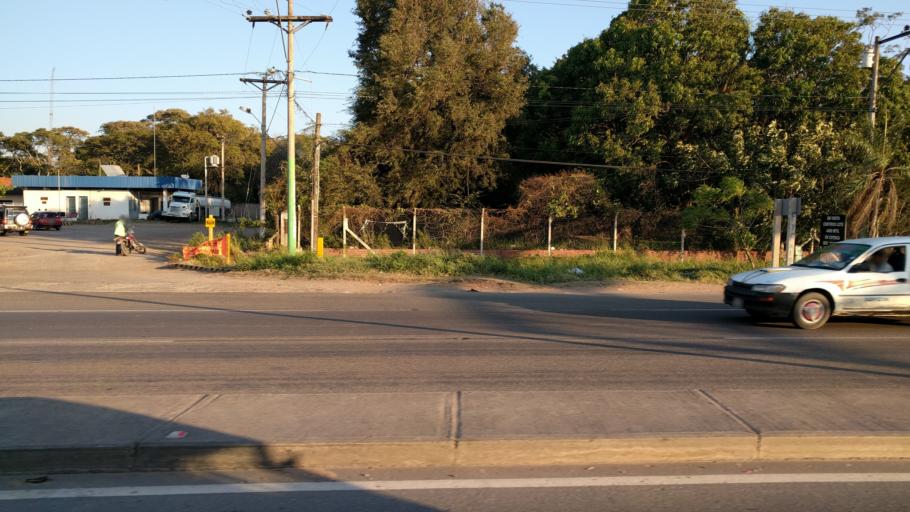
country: BO
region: Santa Cruz
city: Cotoca
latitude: -17.7594
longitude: -63.0144
